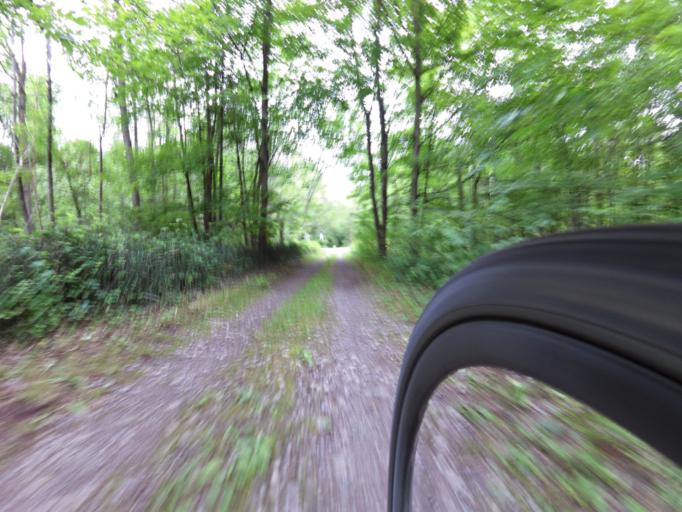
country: CA
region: Ontario
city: Gananoque
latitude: 44.5895
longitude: -76.3075
